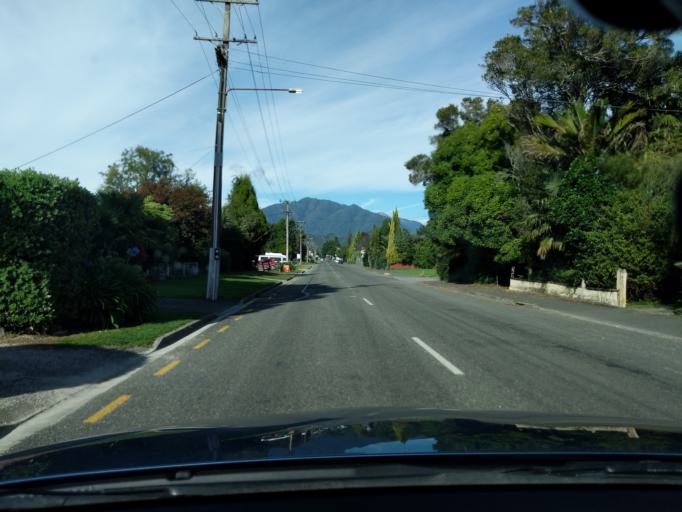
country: NZ
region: Tasman
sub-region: Tasman District
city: Takaka
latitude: -40.8581
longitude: 172.8102
